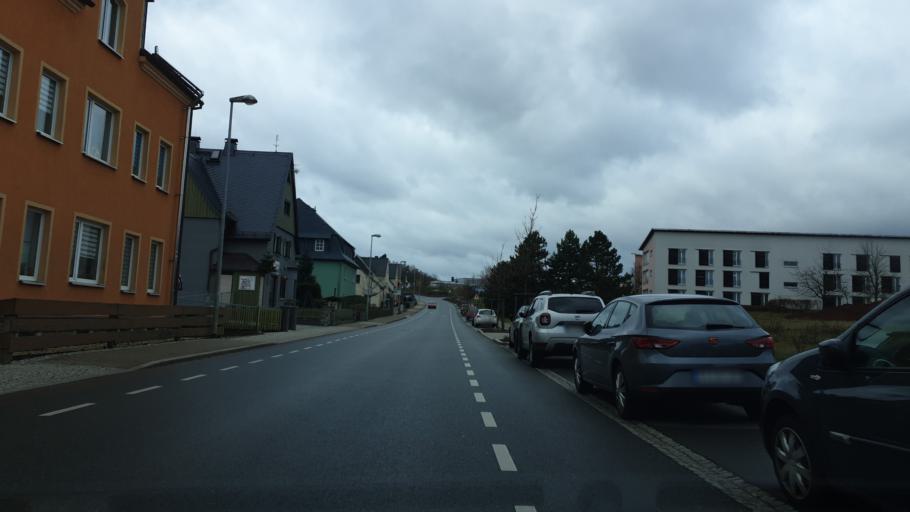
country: DE
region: Saxony
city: Bernsdorf
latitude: 50.7486
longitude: 12.6617
